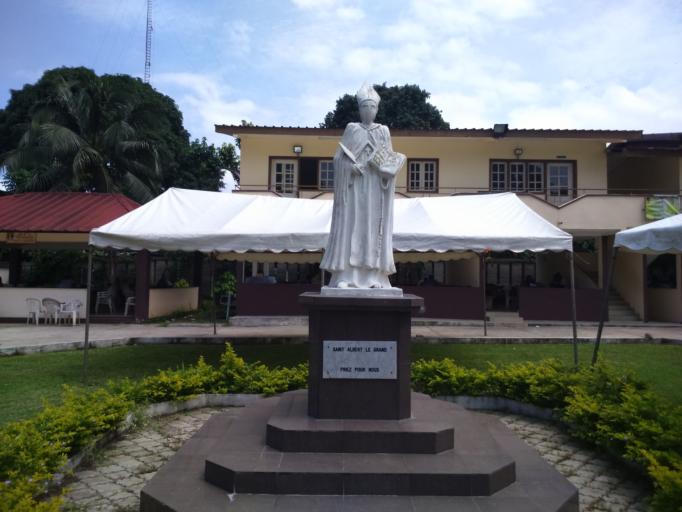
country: CI
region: Lagunes
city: Abidjan
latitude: 5.3476
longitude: -3.9954
